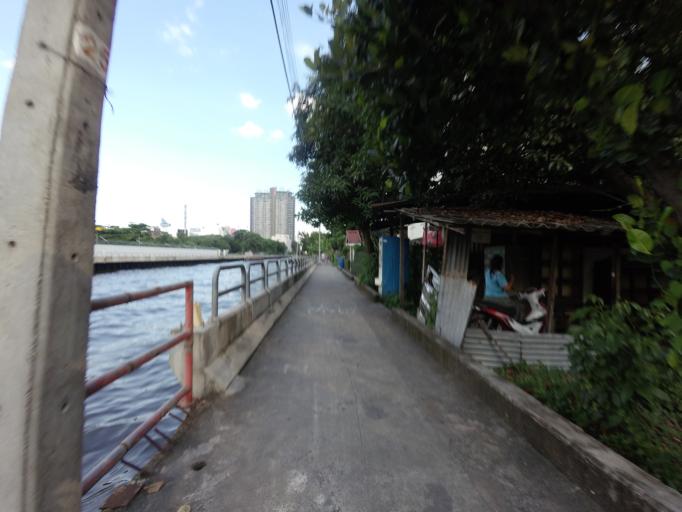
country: TH
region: Bangkok
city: Watthana
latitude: 13.7443
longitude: 100.5805
